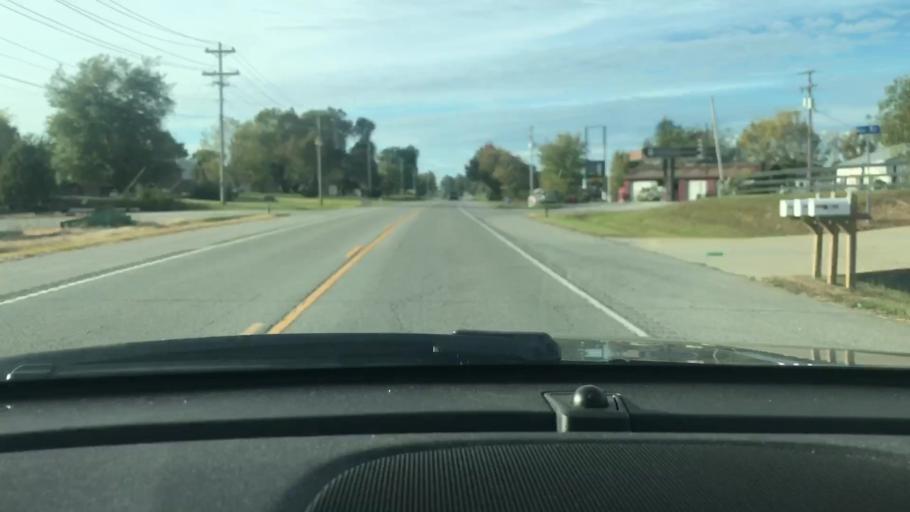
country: US
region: Tennessee
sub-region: Dickson County
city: White Bluff
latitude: 36.1341
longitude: -87.2360
